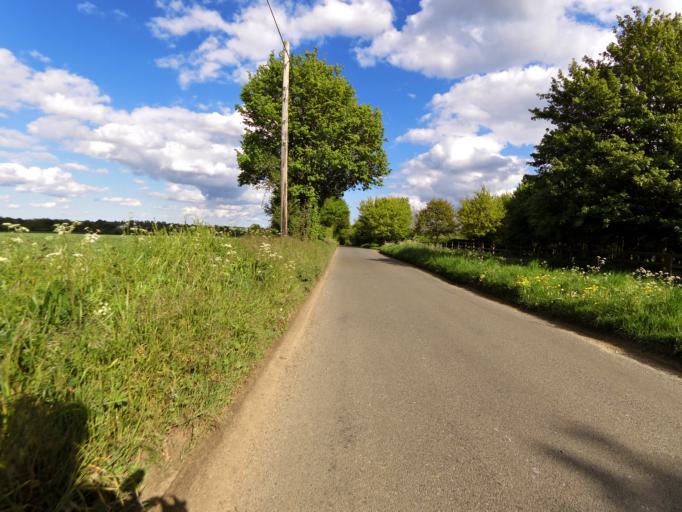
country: GB
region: England
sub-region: Suffolk
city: Woolpit
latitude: 52.2221
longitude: 0.8611
